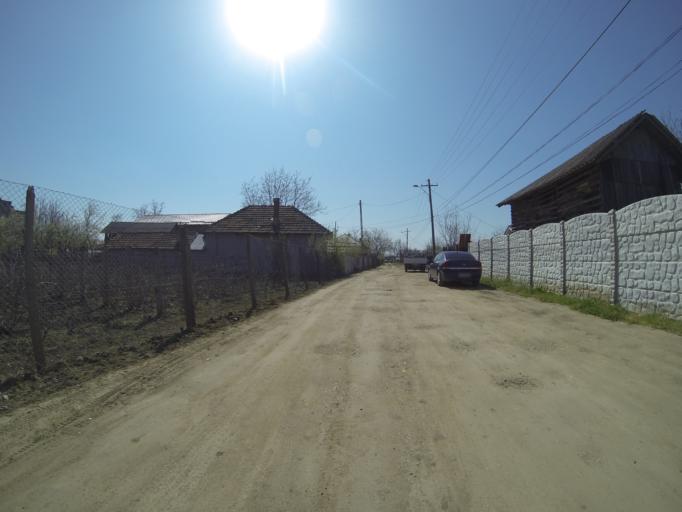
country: RO
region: Dolj
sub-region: Comuna Segarcea
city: Segarcea
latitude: 44.0918
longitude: 23.7318
